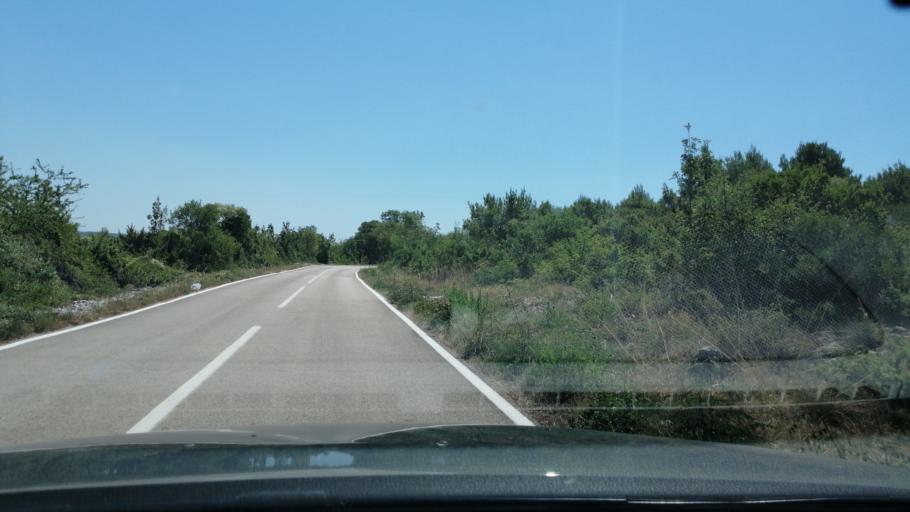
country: HR
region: Sibensko-Kniniska
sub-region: Grad Sibenik
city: Pirovac
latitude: 43.8664
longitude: 15.6866
